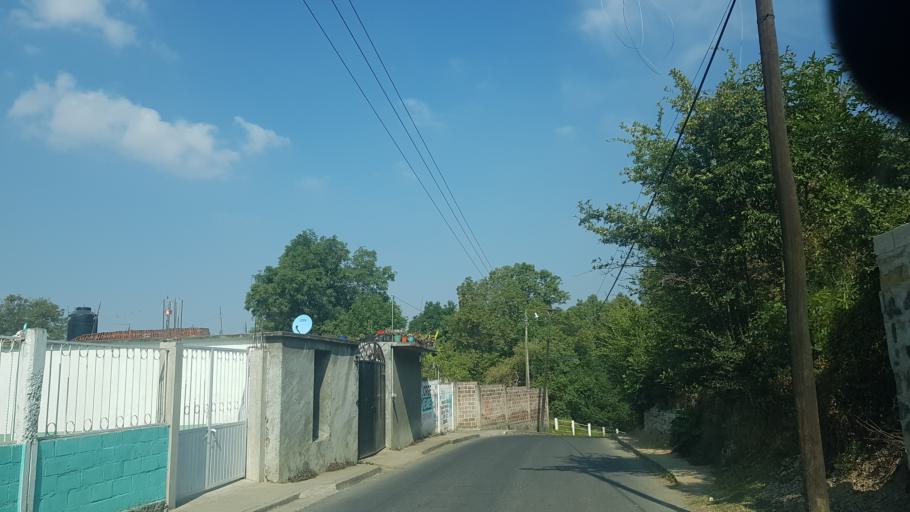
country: MX
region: Morelos
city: Hueyapan
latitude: 18.8881
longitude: -98.6812
